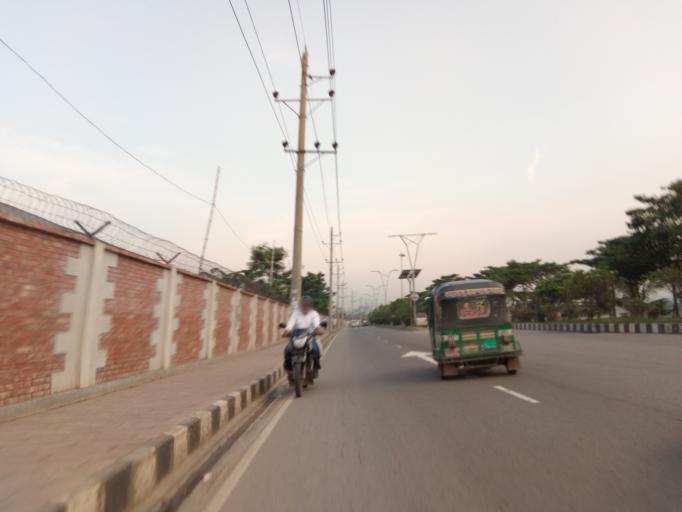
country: BD
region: Dhaka
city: Paltan
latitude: 23.7640
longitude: 90.4119
